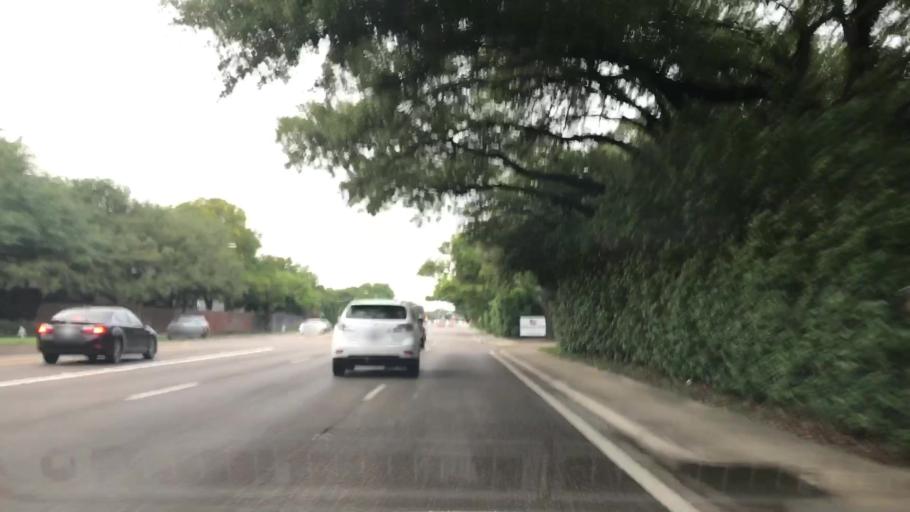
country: US
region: Texas
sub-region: Dallas County
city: University Park
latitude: 32.9030
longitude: -96.8039
